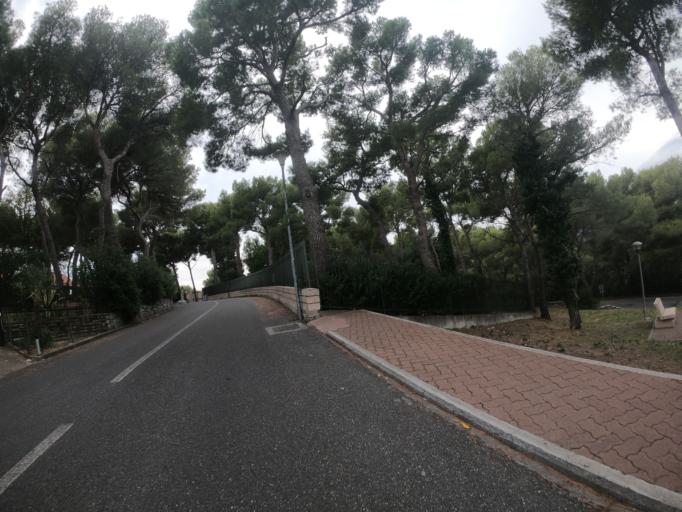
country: IT
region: Liguria
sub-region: Provincia di Savona
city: Marina di Andora
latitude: 43.9561
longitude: 8.1563
